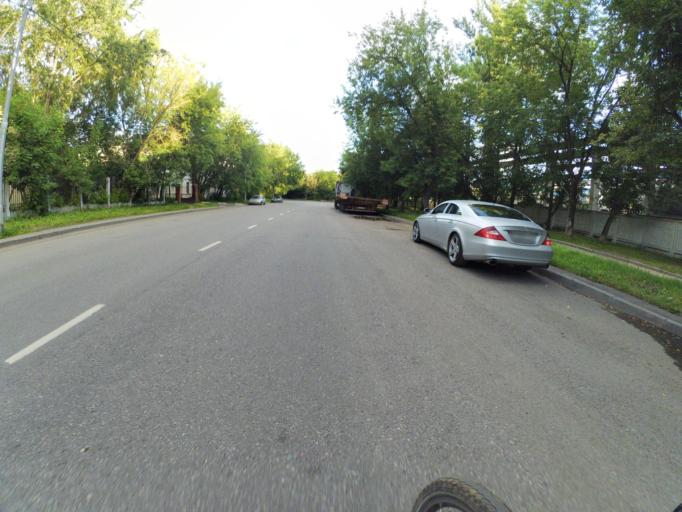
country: RU
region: Moscow
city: Strogino
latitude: 55.8350
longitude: 37.4251
